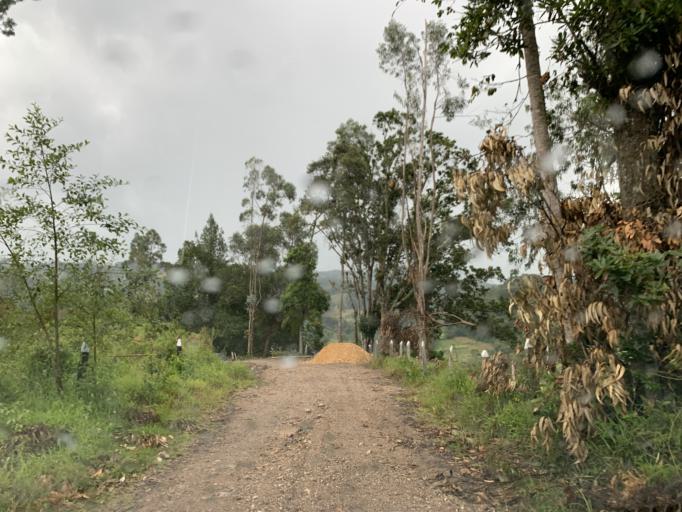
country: CO
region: Boyaca
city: Arcabuco
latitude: 5.7549
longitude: -73.4753
